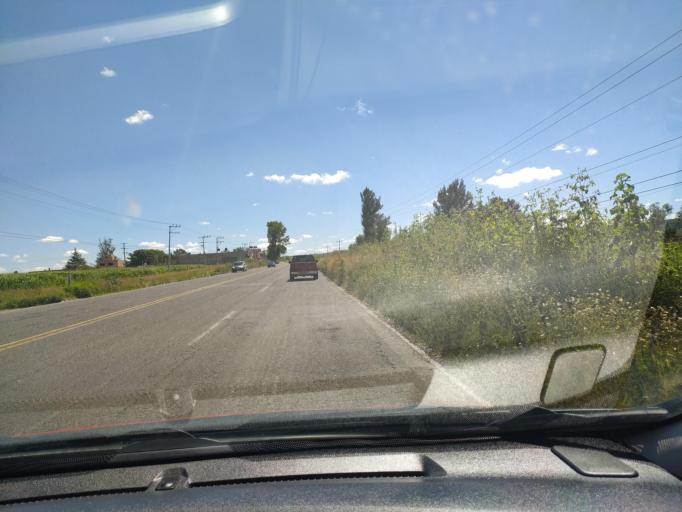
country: MX
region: Jalisco
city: San Miguel el Alto
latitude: 21.0266
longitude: -102.3734
